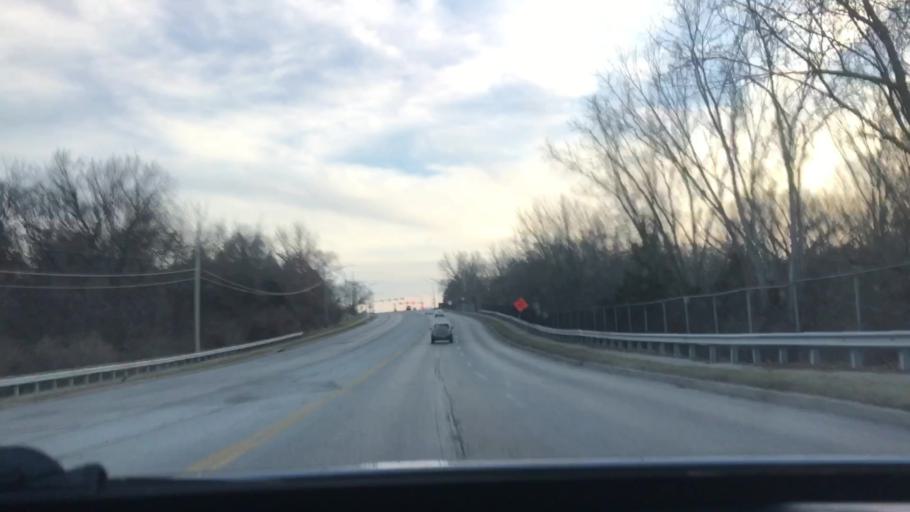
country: US
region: Missouri
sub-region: Jackson County
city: Independence
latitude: 39.0380
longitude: -94.3878
